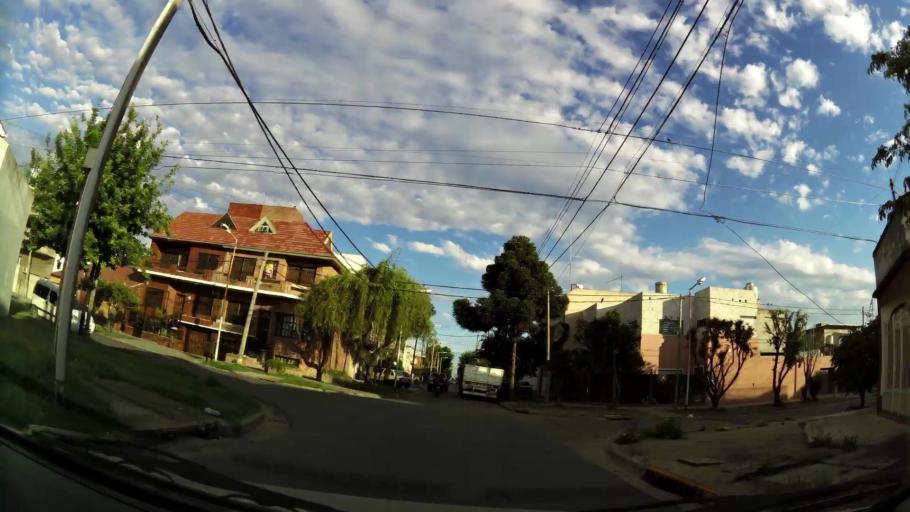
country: AR
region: Buenos Aires
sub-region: Partido de Avellaneda
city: Avellaneda
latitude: -34.6866
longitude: -58.3461
